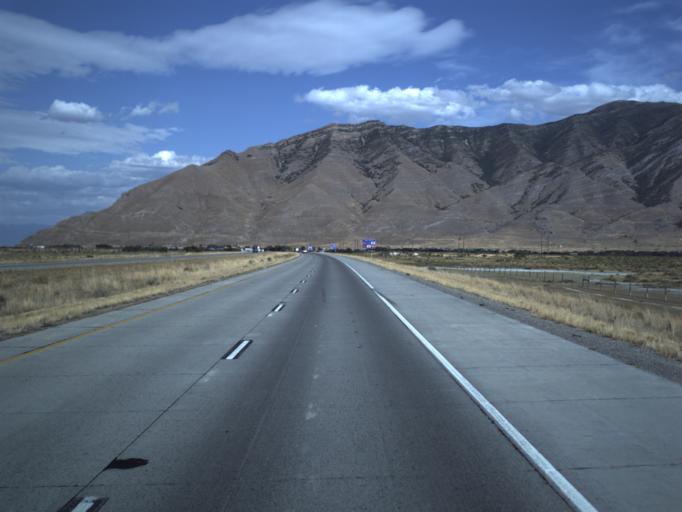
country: US
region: Utah
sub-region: Tooele County
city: Stansbury park
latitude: 40.6704
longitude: -112.2968
